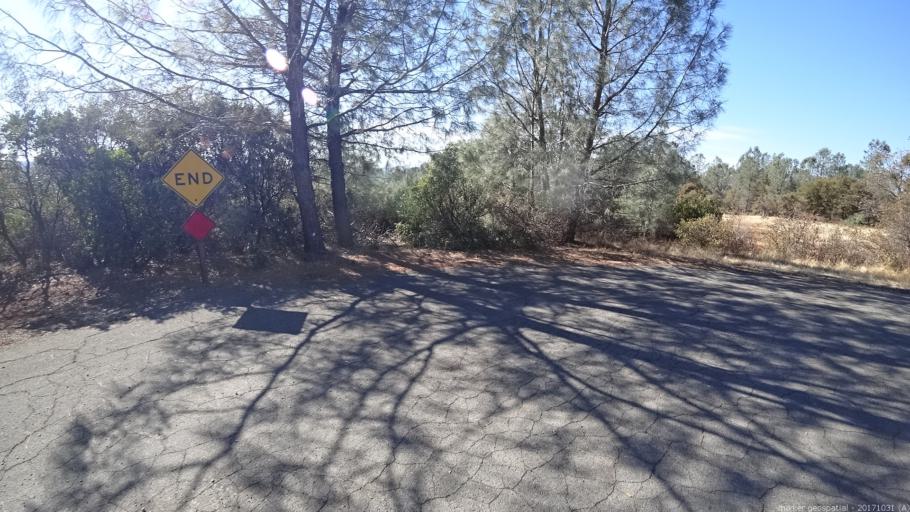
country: US
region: California
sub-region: Shasta County
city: Shingletown
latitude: 40.5121
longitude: -122.0287
